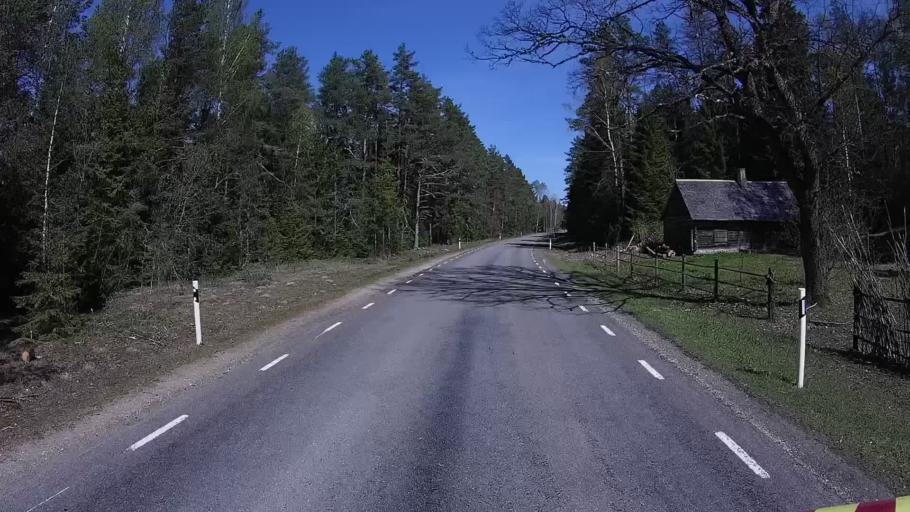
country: EE
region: Harju
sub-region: Nissi vald
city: Turba
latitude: 59.1272
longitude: 24.0674
